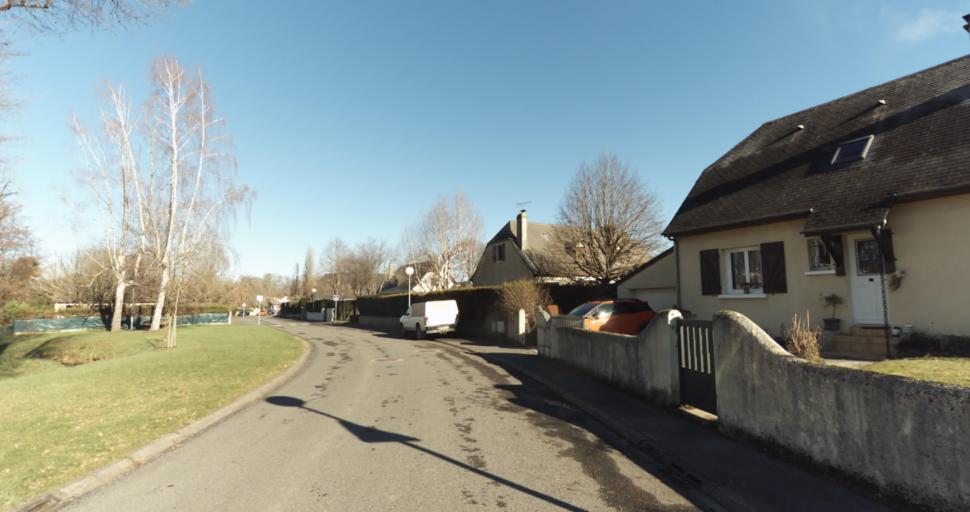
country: FR
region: Aquitaine
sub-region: Departement des Pyrenees-Atlantiques
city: Morlaas
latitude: 43.3454
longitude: -0.2601
